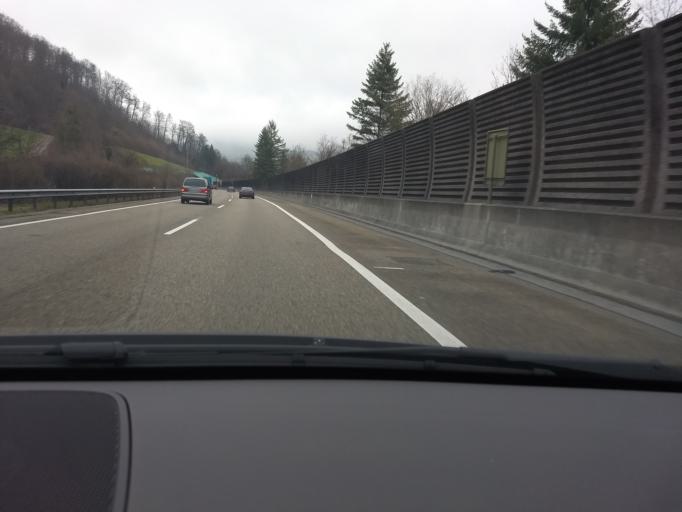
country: CH
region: Basel-Landschaft
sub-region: Bezirk Sissach
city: Sissach
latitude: 47.4580
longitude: 7.8031
